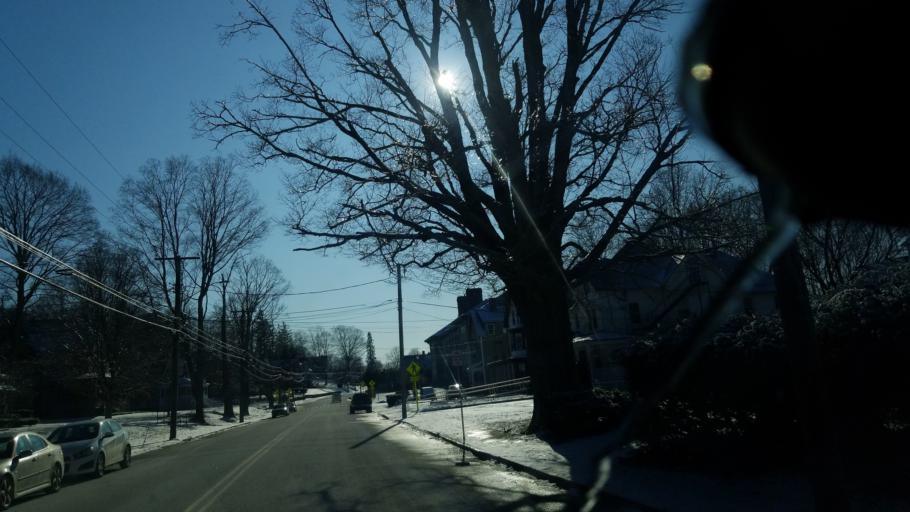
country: US
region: Connecticut
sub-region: Windham County
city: Danielson
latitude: 41.8053
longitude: -71.8799
